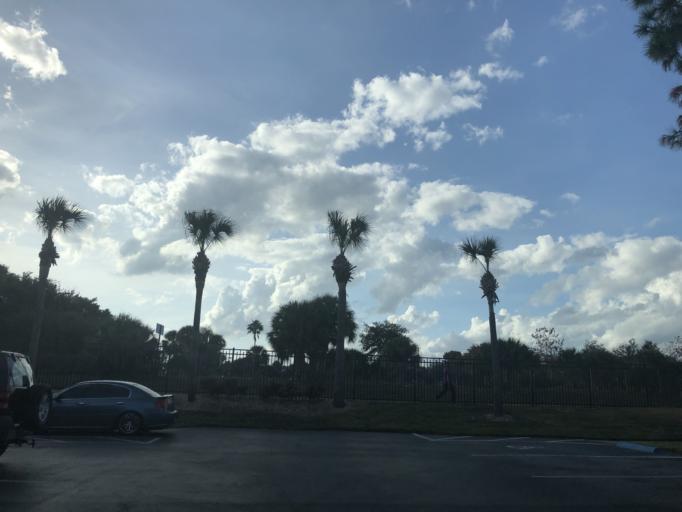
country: US
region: Florida
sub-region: Orange County
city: Tangelo Park
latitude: 28.4513
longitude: -81.4678
